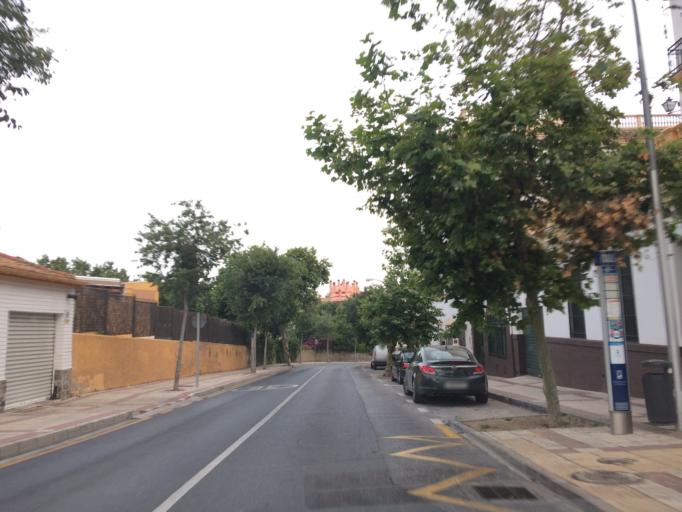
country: ES
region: Andalusia
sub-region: Provincia de Malaga
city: Malaga
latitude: 36.7242
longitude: -4.3997
